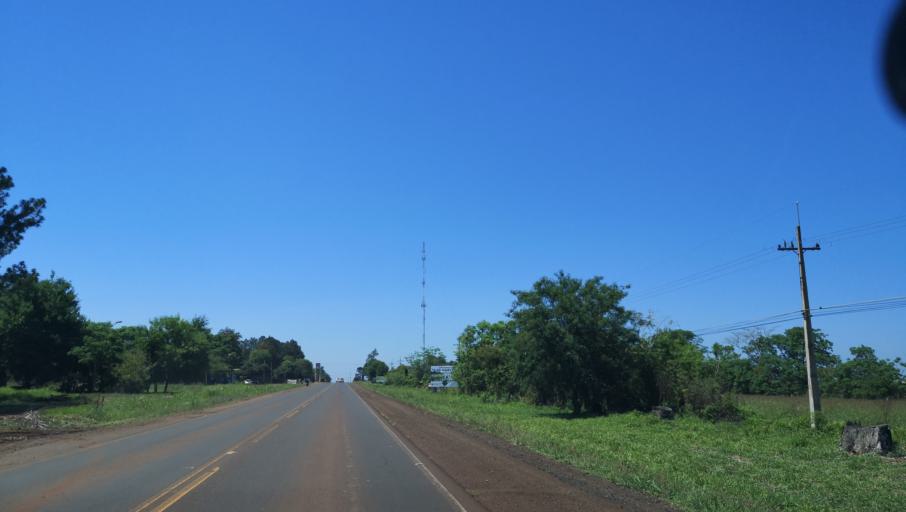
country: PY
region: Itapua
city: San Juan del Parana
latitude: -27.2631
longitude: -55.9629
